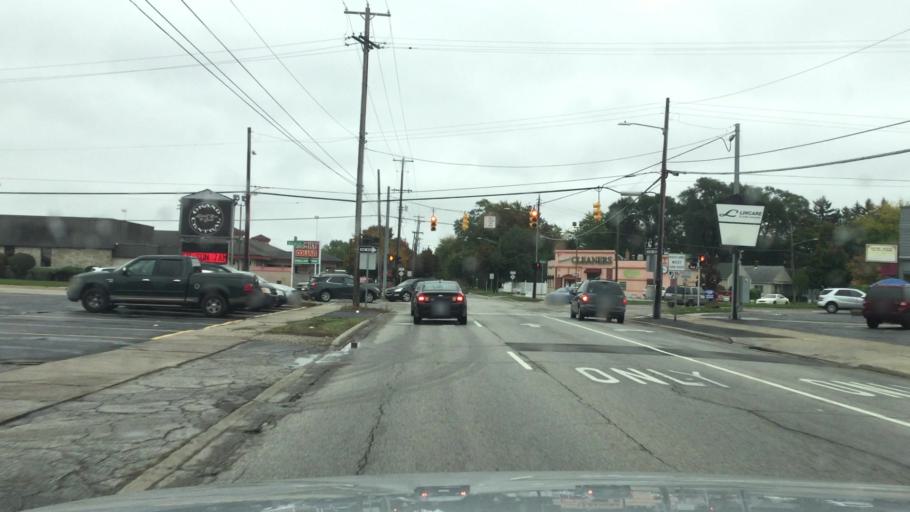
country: US
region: Michigan
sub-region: Saginaw County
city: Saginaw
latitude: 43.4367
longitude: -83.9908
